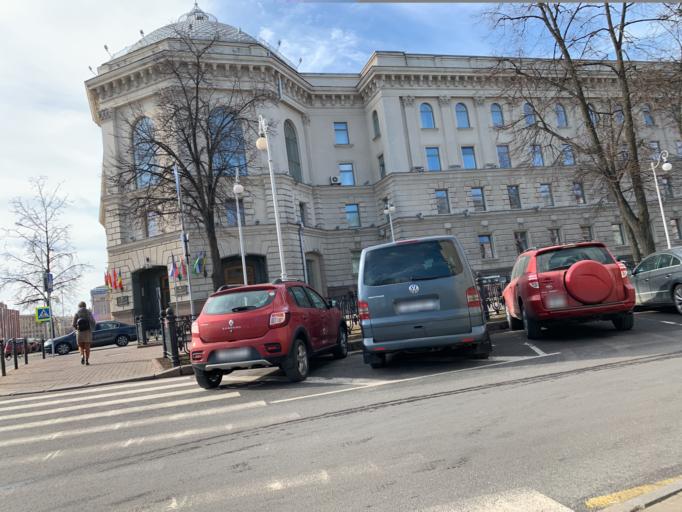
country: BY
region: Minsk
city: Minsk
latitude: 53.8968
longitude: 27.5582
